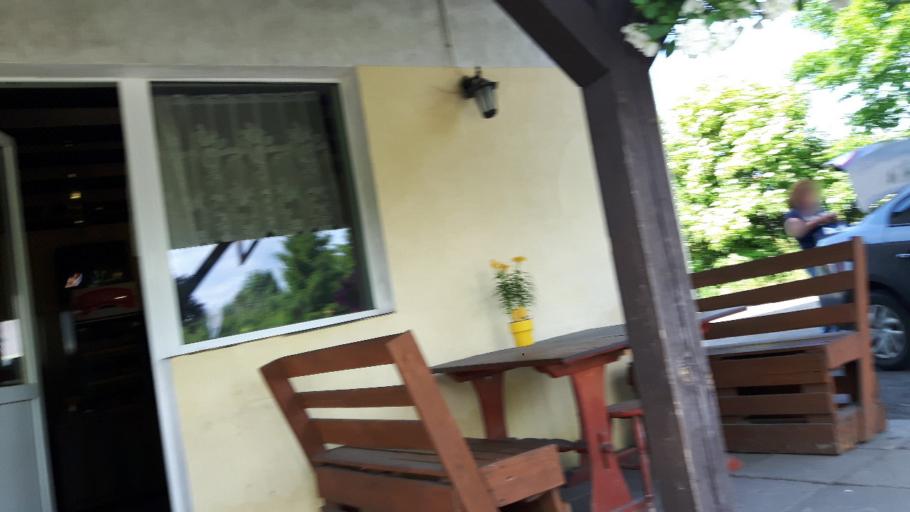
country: RU
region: Kaliningrad
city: Mamonovo
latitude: 54.4295
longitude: 19.8915
